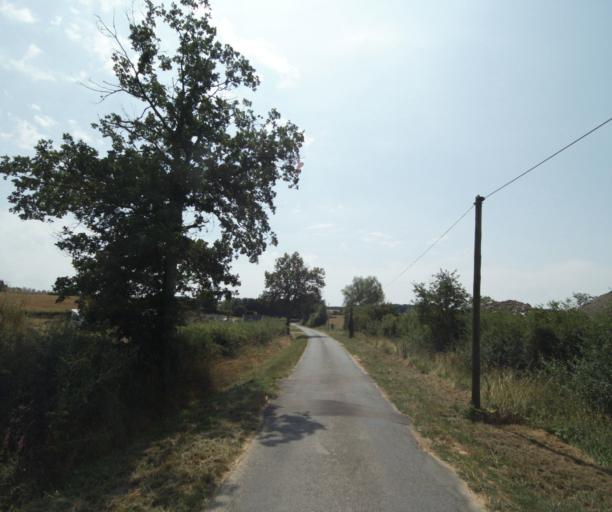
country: FR
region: Bourgogne
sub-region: Departement de Saone-et-Loire
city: Gueugnon
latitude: 46.5696
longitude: 4.0593
